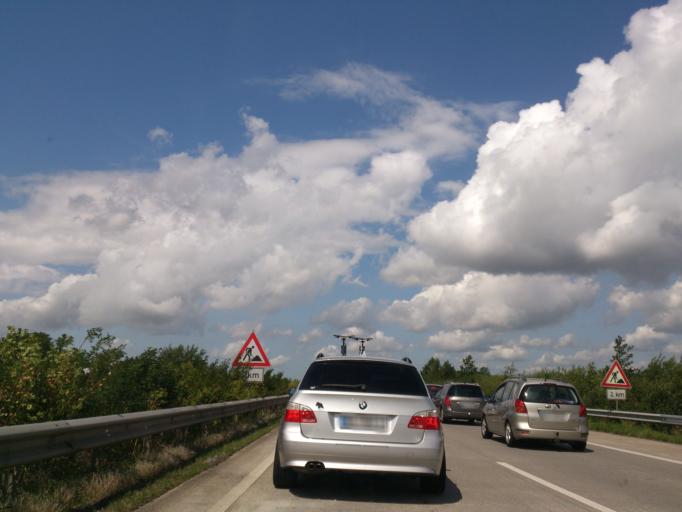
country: DE
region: Schleswig-Holstein
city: Dageling
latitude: 53.8888
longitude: 9.5340
